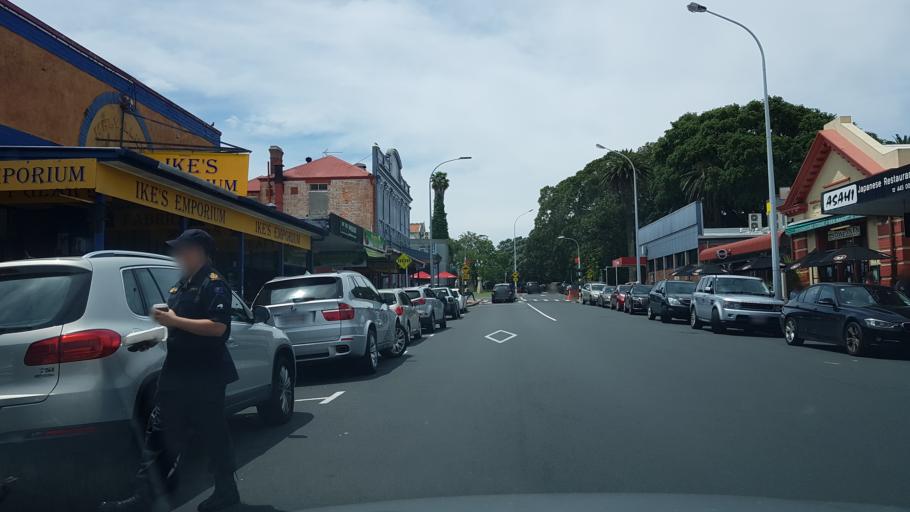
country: NZ
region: Auckland
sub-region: Auckland
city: Auckland
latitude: -36.8303
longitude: 174.7967
